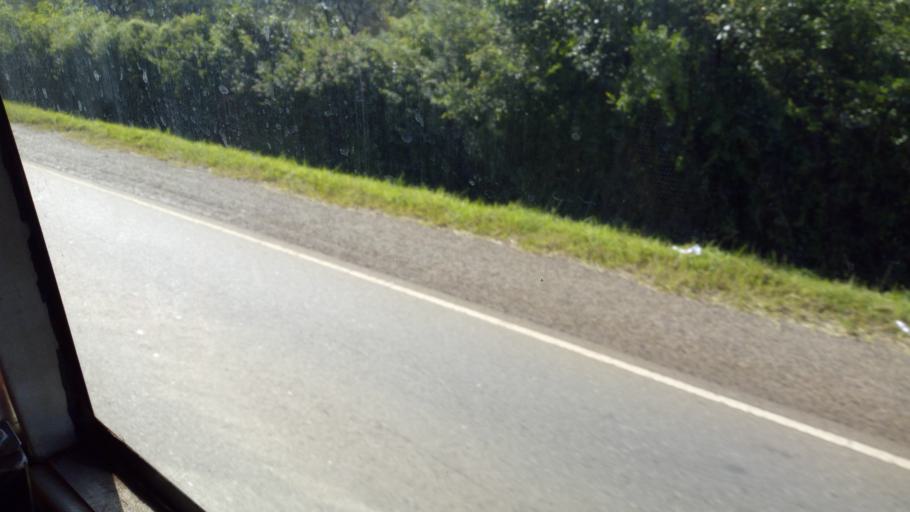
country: UG
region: Central Region
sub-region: Lyantonde District
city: Lyantonde
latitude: -0.4260
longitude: 31.1081
